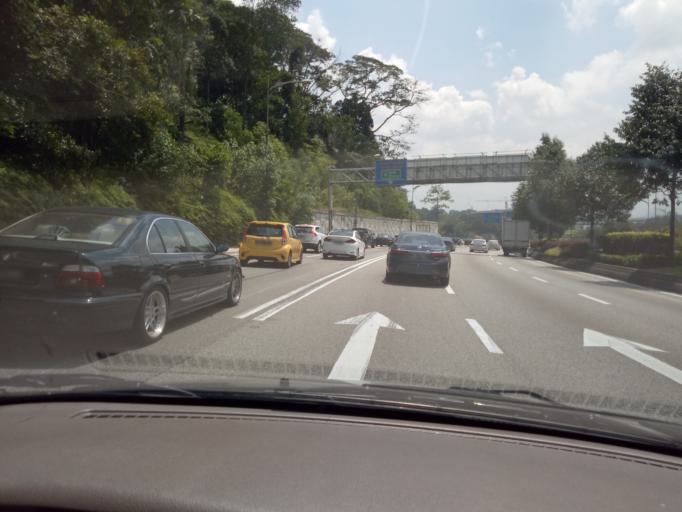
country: MY
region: Kuala Lumpur
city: Kuala Lumpur
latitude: 3.1435
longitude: 101.6784
